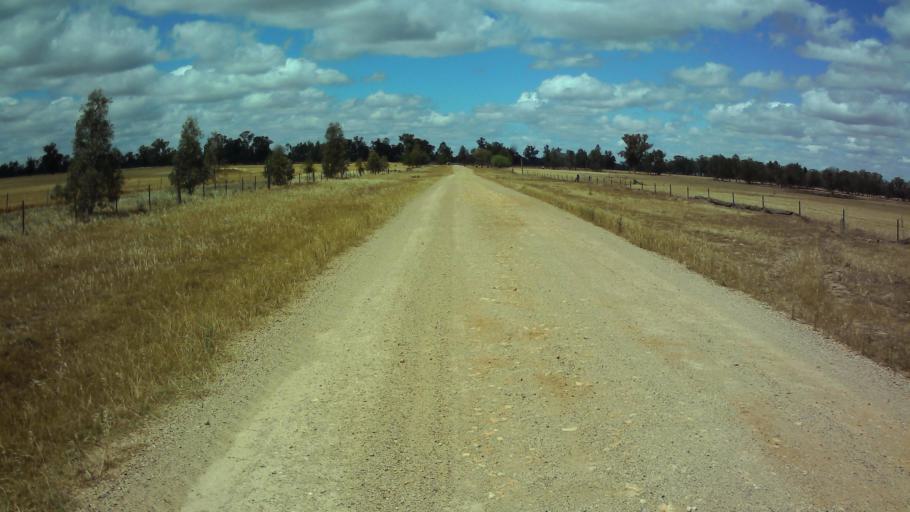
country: AU
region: New South Wales
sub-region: Weddin
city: Grenfell
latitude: -34.0113
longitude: 147.9163
